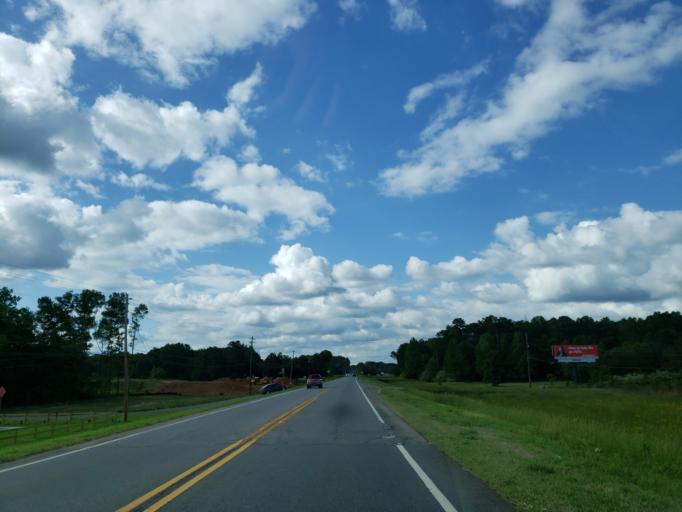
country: US
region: Georgia
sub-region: Bartow County
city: Cartersville
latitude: 34.2358
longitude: -84.8565
